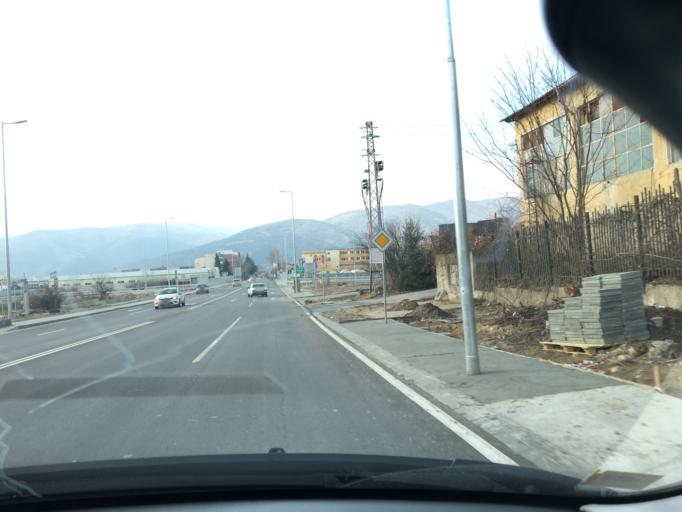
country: BG
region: Blagoevgrad
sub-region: Obshtina Sandanski
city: Sandanski
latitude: 41.5423
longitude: 23.2585
